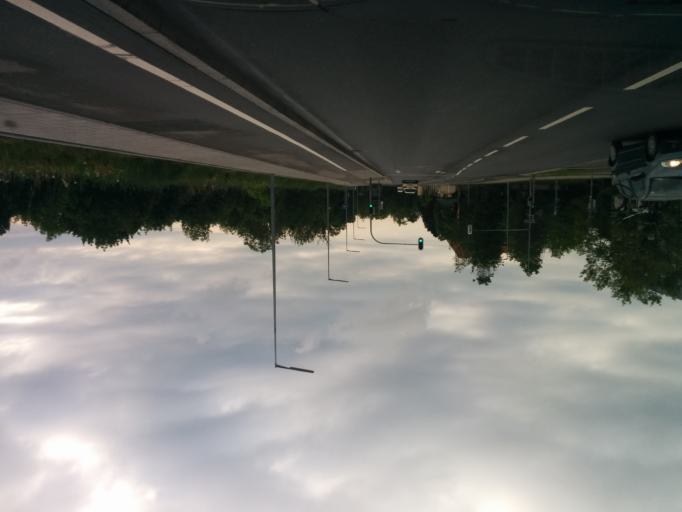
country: DE
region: Bavaria
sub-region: Upper Bavaria
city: Pullach im Isartal
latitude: 48.0924
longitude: 11.5397
